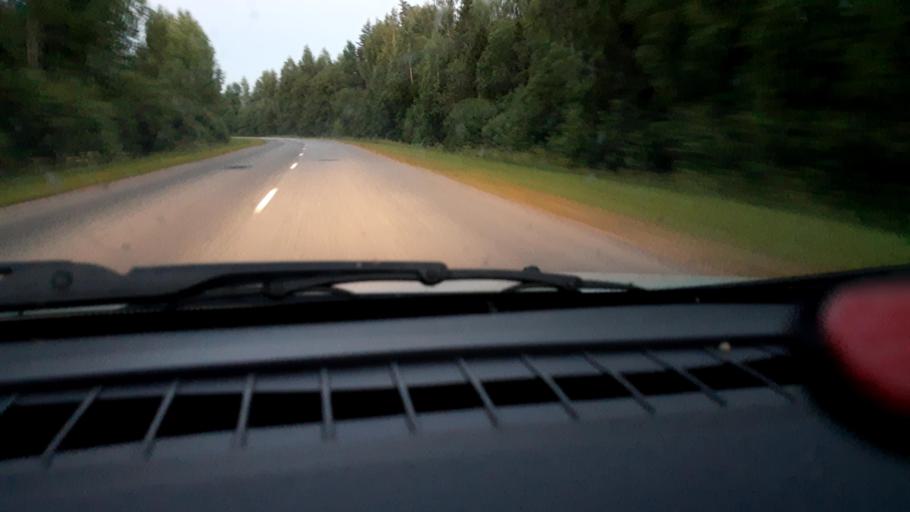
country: RU
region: Nizjnij Novgorod
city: Prudy
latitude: 57.3645
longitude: 46.1815
